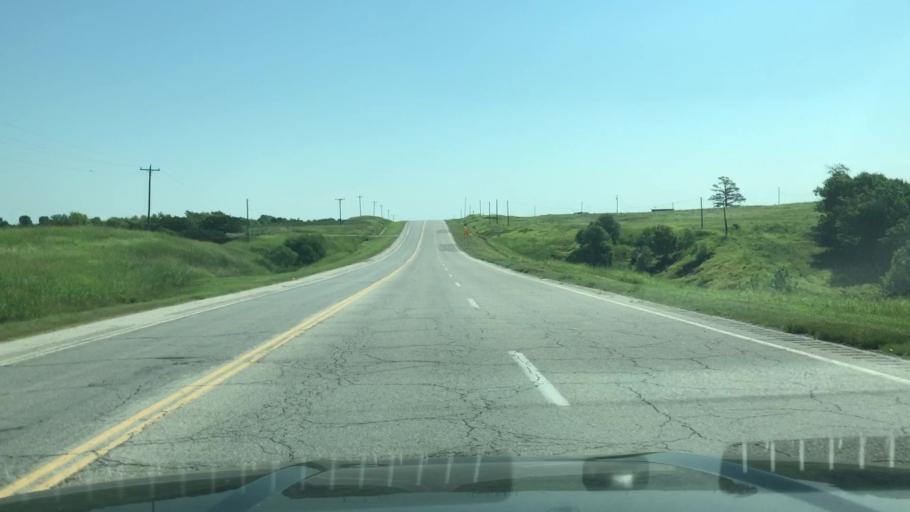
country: US
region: Oklahoma
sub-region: Creek County
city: Drumright
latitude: 35.9917
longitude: -96.5382
